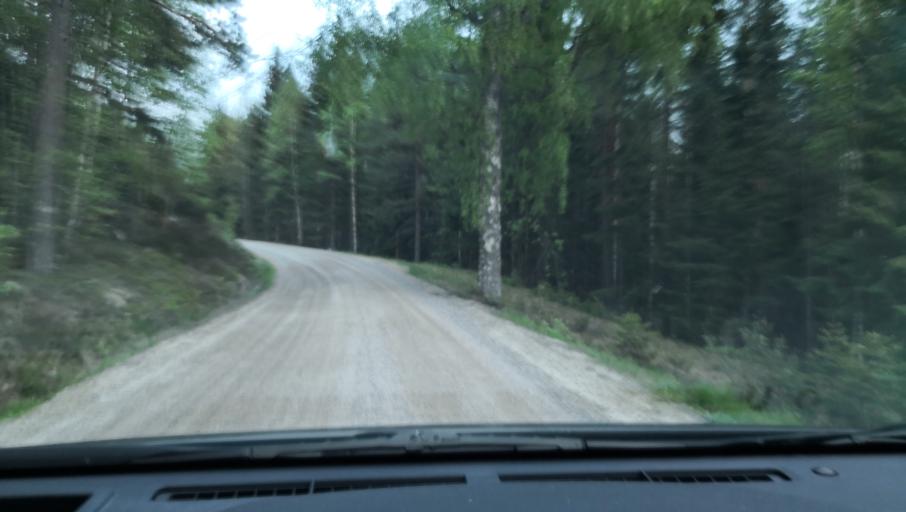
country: SE
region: Vaestmanland
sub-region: Skinnskattebergs Kommun
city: Skinnskatteberg
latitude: 59.7491
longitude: 15.4598
